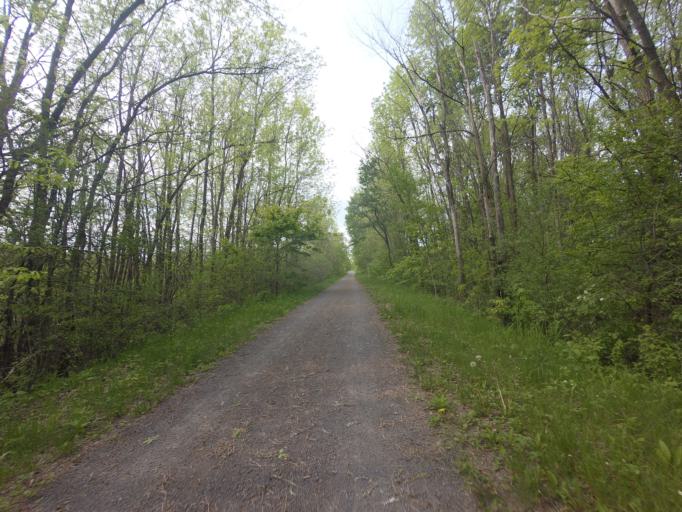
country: CA
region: Ontario
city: Kingston
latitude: 44.3198
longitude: -76.5869
